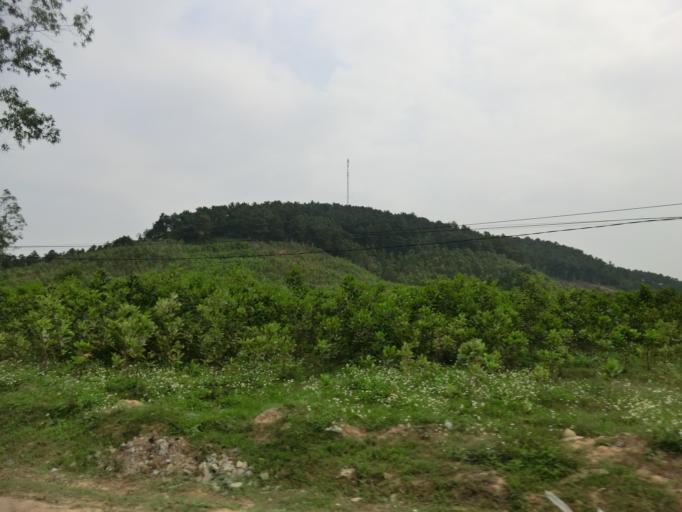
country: VN
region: Nghe An
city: Cau Giat
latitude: 19.1914
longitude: 105.5860
